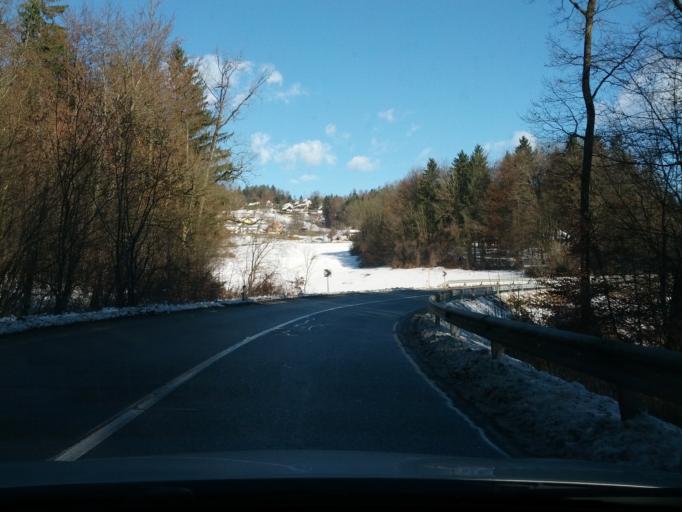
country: SI
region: Lukovica
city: Lukovica pri Domzalah
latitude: 46.1372
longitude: 14.7032
